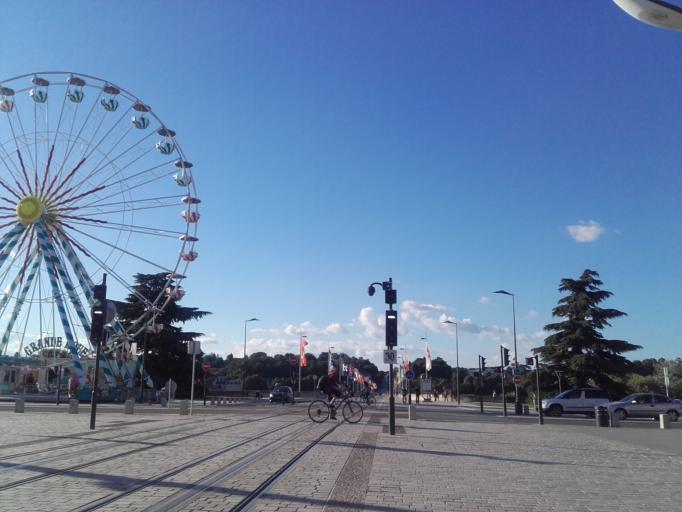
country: FR
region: Centre
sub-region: Departement d'Indre-et-Loire
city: Tours
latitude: 47.3964
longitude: 0.6864
